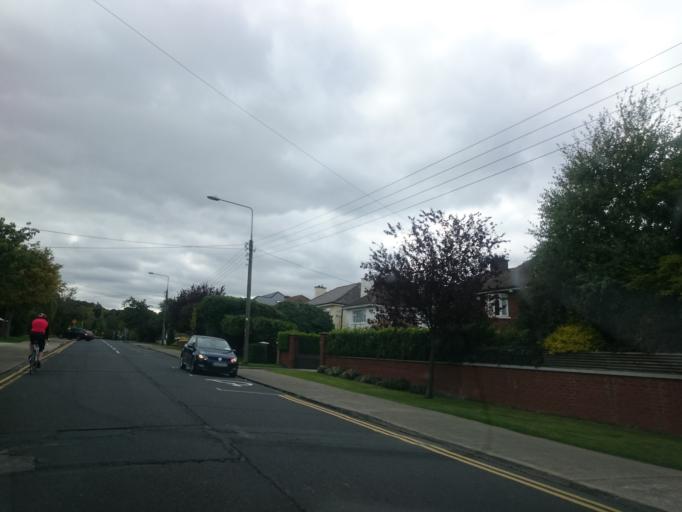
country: IE
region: Leinster
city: Donnybrook
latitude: 53.3101
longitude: -6.2144
